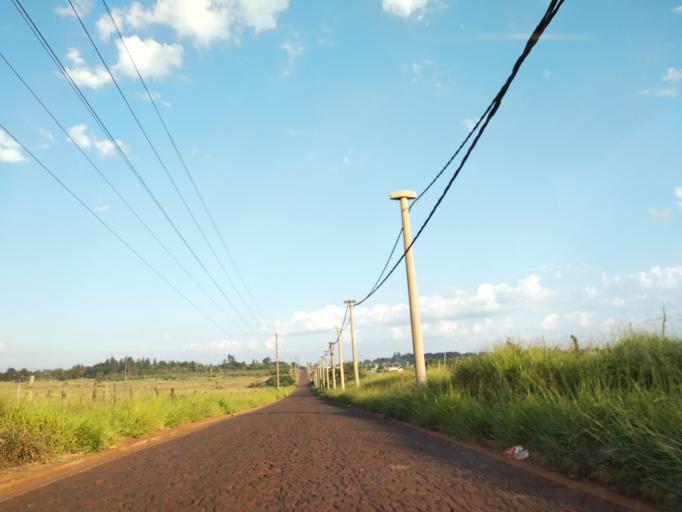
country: AR
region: Misiones
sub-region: Departamento de Capital
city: Posadas
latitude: -27.4429
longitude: -55.9356
